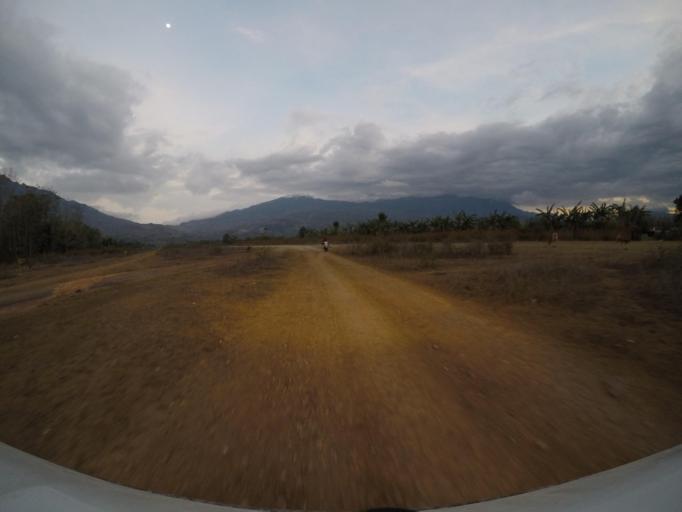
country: TL
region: Bobonaro
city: Maliana
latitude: -8.9708
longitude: 125.2124
